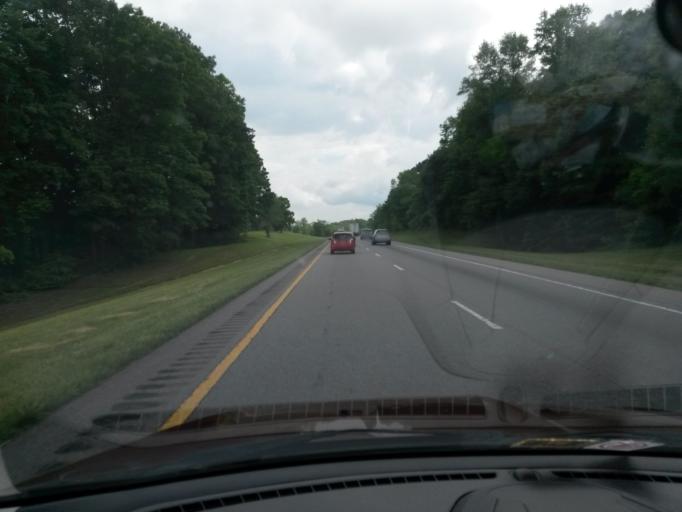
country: US
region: North Carolina
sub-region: Iredell County
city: Statesville
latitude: 35.9837
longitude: -80.8391
